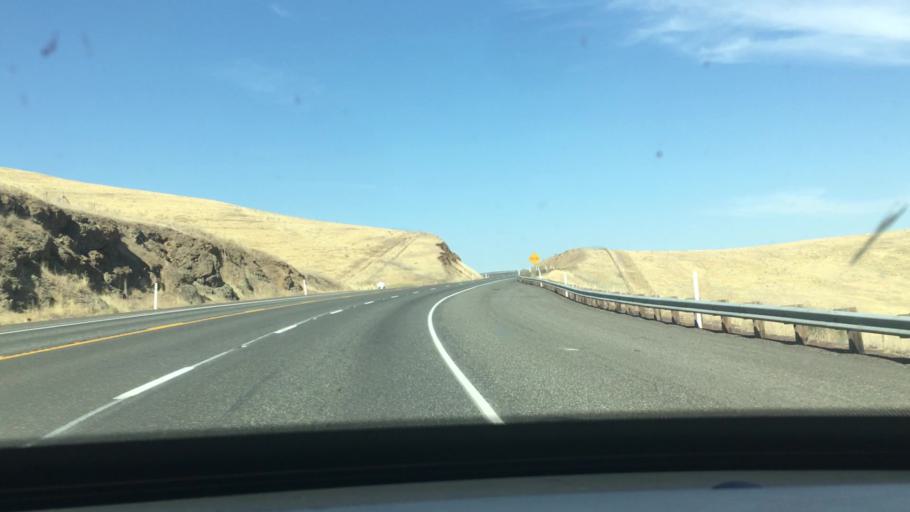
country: US
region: Washington
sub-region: Klickitat County
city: Goldendale
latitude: 45.7082
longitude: -120.8070
